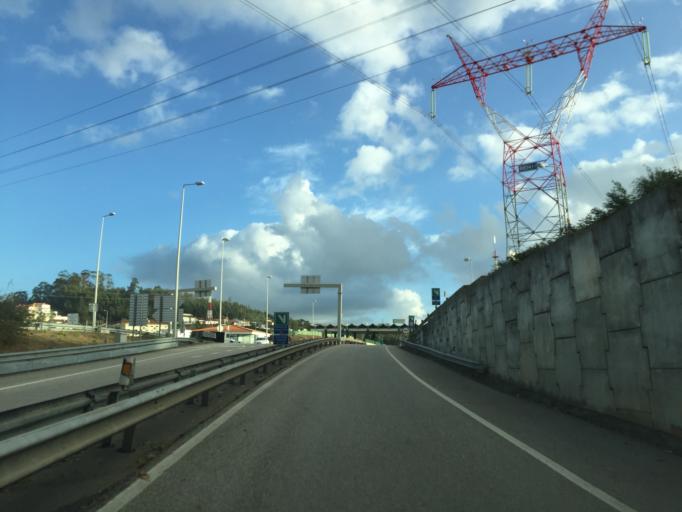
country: PT
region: Coimbra
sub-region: Coimbra
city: Coimbra
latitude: 40.2020
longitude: -8.4907
